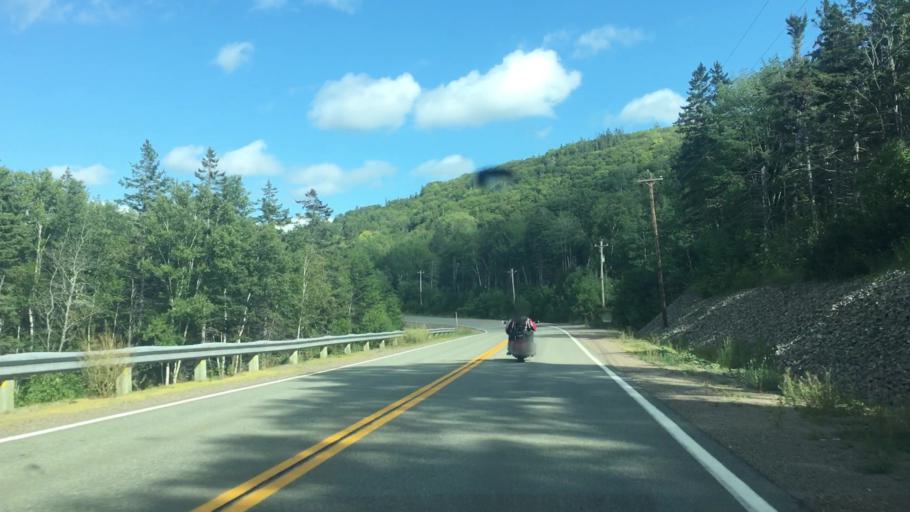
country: CA
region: Nova Scotia
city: Sydney
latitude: 45.8498
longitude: -60.6423
